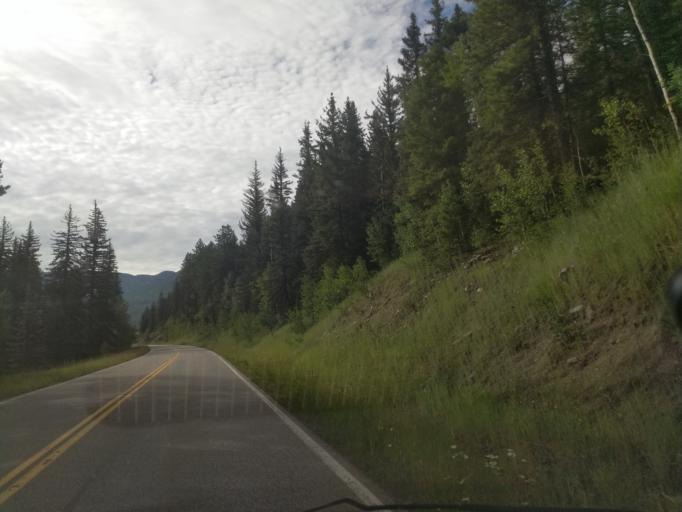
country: US
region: Colorado
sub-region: Garfield County
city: Carbondale
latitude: 39.0889
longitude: -107.2495
